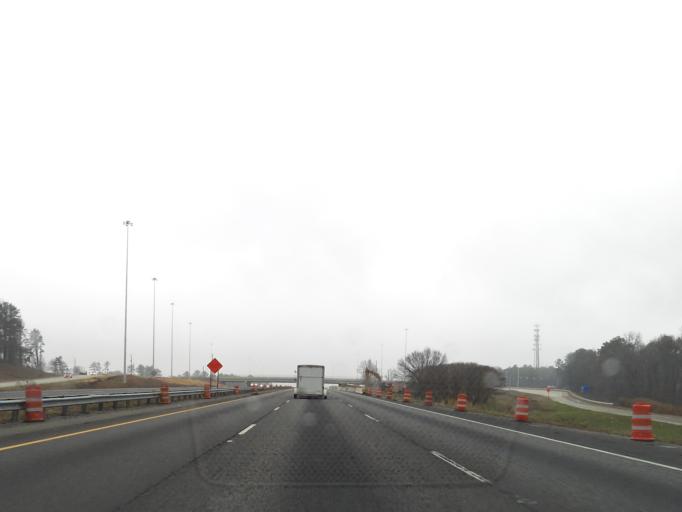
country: US
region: Georgia
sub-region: Henry County
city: Stockbridge
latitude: 33.4780
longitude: -84.2160
